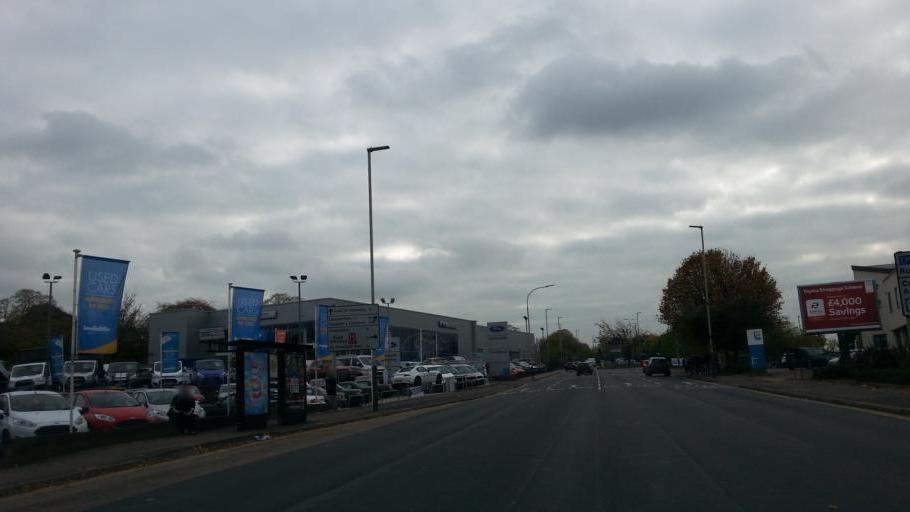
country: GB
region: England
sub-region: City of Leicester
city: Leicester
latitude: 52.6234
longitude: -1.1313
